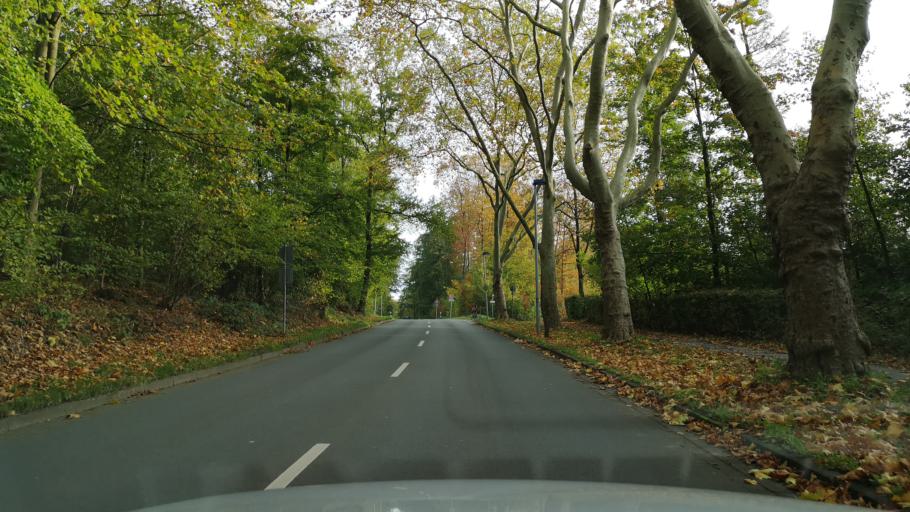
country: DE
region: North Rhine-Westphalia
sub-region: Regierungsbezirk Arnsberg
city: Menden
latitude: 51.4331
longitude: 7.8122
